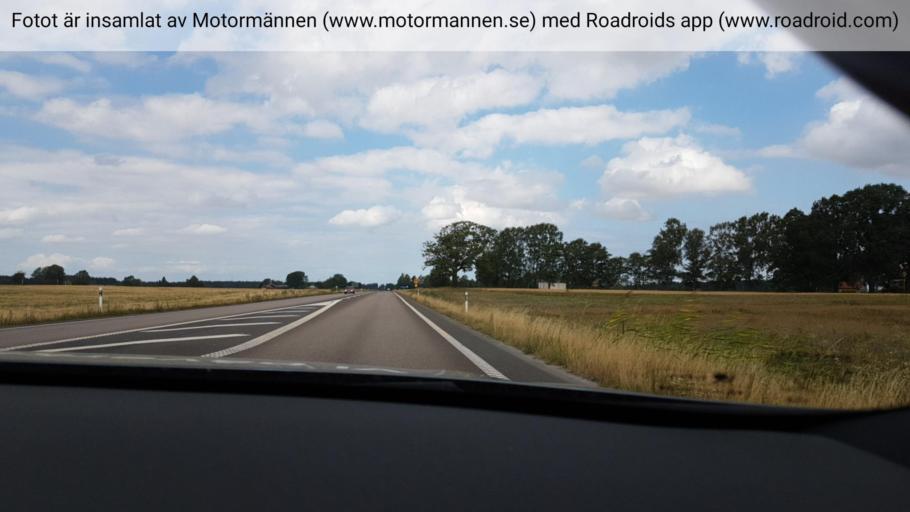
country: SE
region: Vaestra Goetaland
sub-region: Skara Kommun
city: Skara
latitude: 58.4022
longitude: 13.3949
